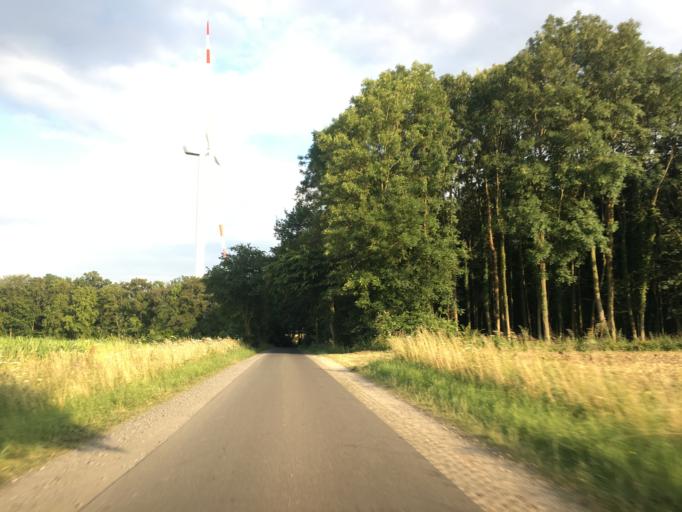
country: DE
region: North Rhine-Westphalia
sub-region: Regierungsbezirk Munster
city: Muenster
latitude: 51.9673
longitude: 7.5407
